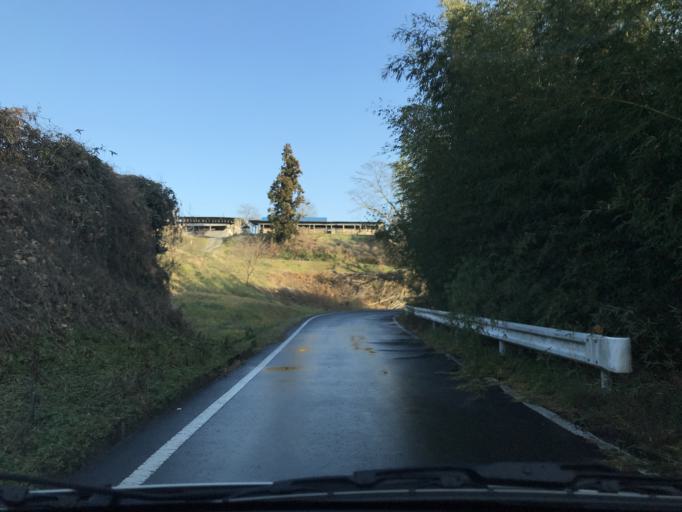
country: JP
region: Miyagi
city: Wakuya
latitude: 38.7025
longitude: 141.1326
